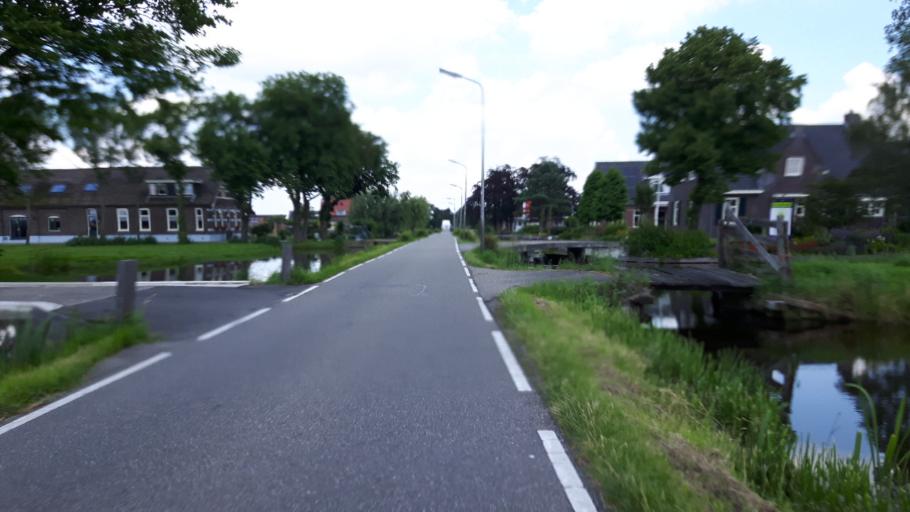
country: NL
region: South Holland
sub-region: Gemeente Gouda
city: Bloemendaal
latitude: 52.0400
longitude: 4.6879
